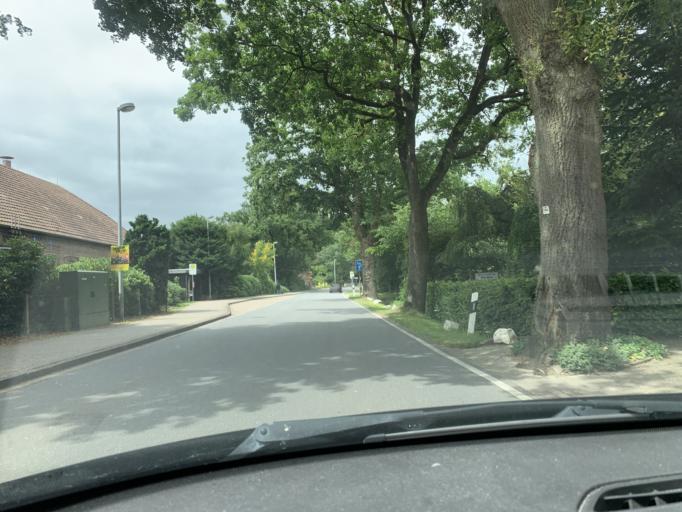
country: DE
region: Lower Saxony
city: Wiefelstede
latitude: 53.1987
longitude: 8.1259
